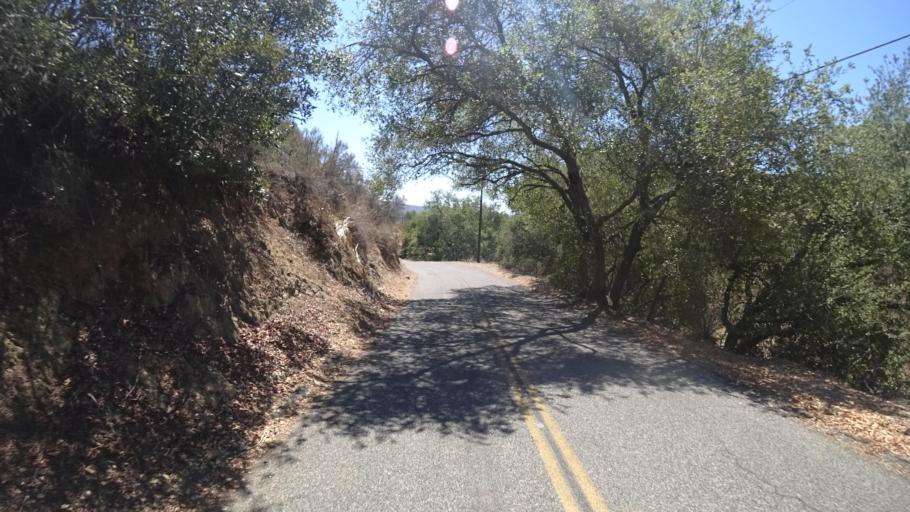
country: US
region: California
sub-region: San Diego County
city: Rainbow
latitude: 33.3881
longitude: -117.0416
